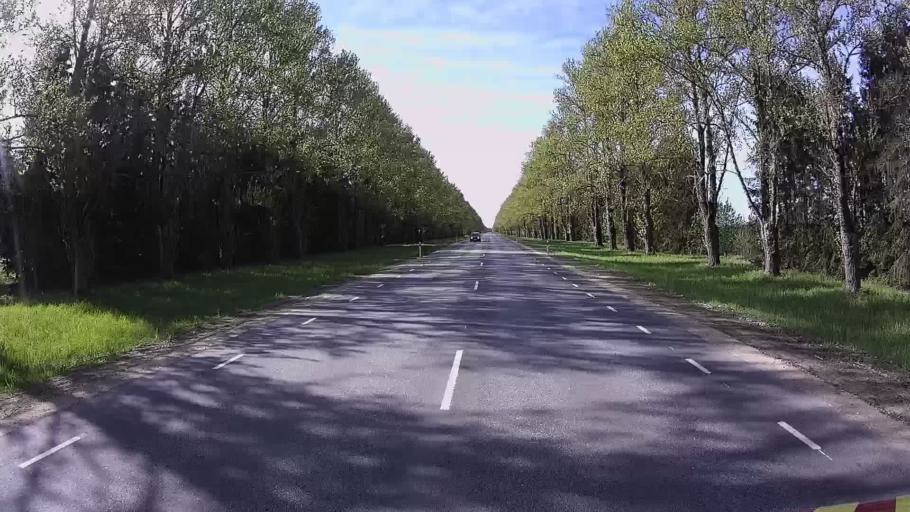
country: EE
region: Polvamaa
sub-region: Polva linn
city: Polva
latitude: 58.2936
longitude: 27.0016
